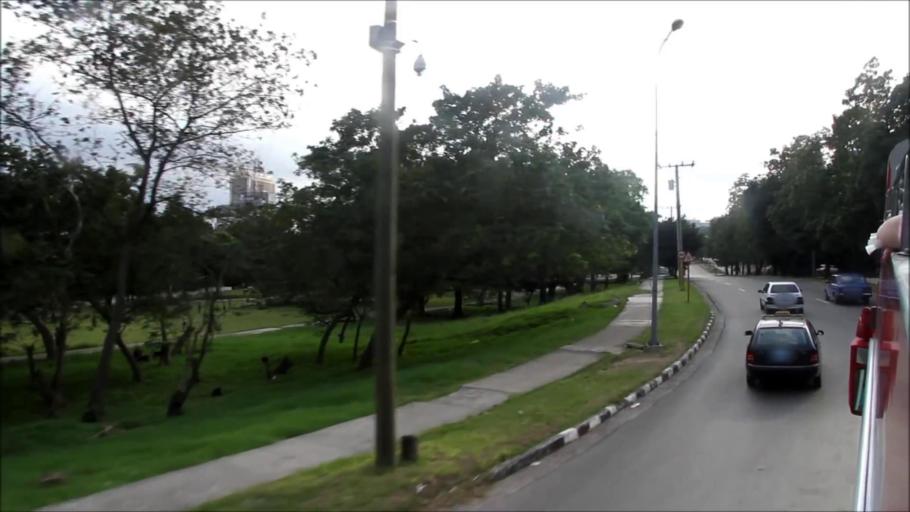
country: CU
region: La Habana
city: Havana
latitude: 23.1289
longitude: -82.3853
